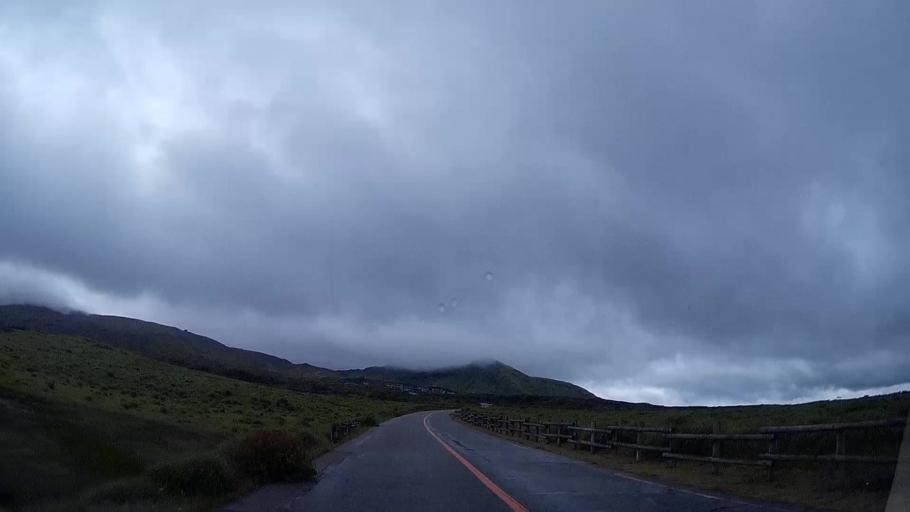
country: JP
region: Kumamoto
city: Aso
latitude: 32.8834
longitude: 131.0662
